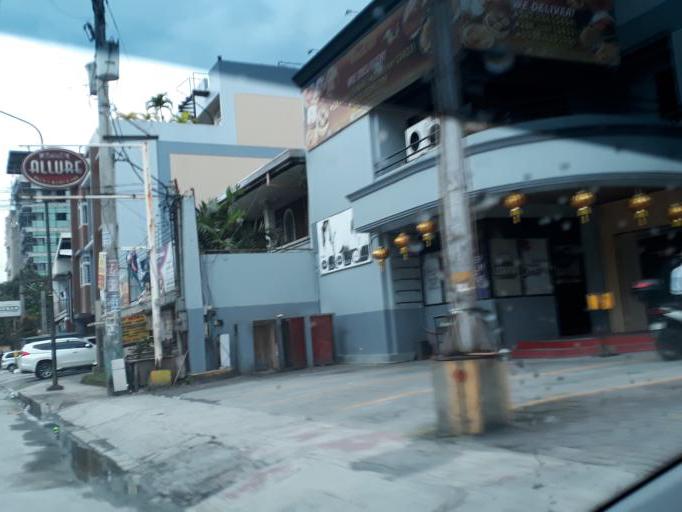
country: PH
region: Calabarzon
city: Del Monte
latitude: 14.6404
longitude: 121.0006
